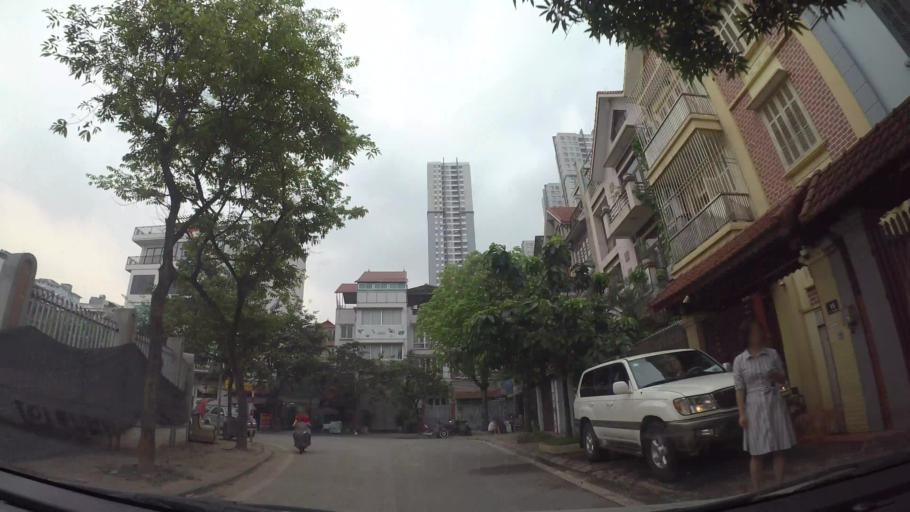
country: VN
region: Ha Noi
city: Cau Dien
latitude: 21.0342
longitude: 105.7629
